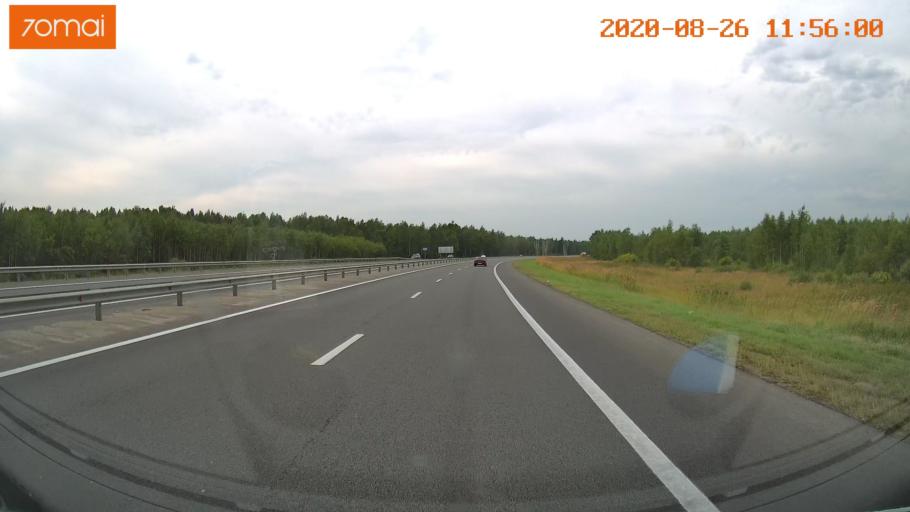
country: RU
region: Rjazan
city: Kiritsy
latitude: 54.2657
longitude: 40.3870
